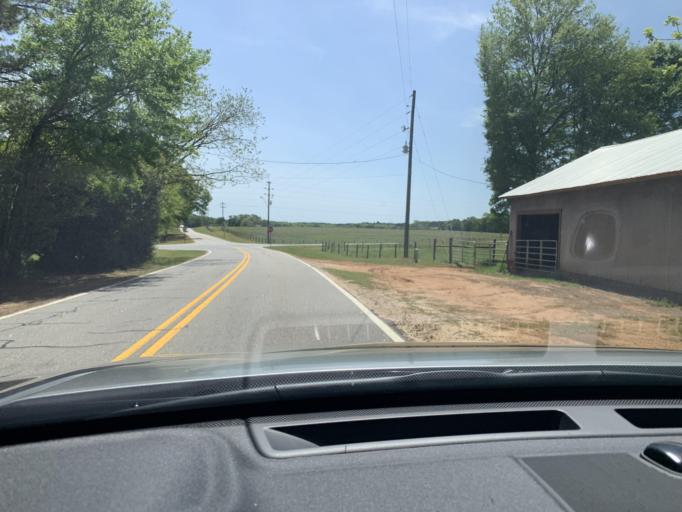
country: US
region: Georgia
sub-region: Oconee County
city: Bogart
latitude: 33.8569
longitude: -83.5490
